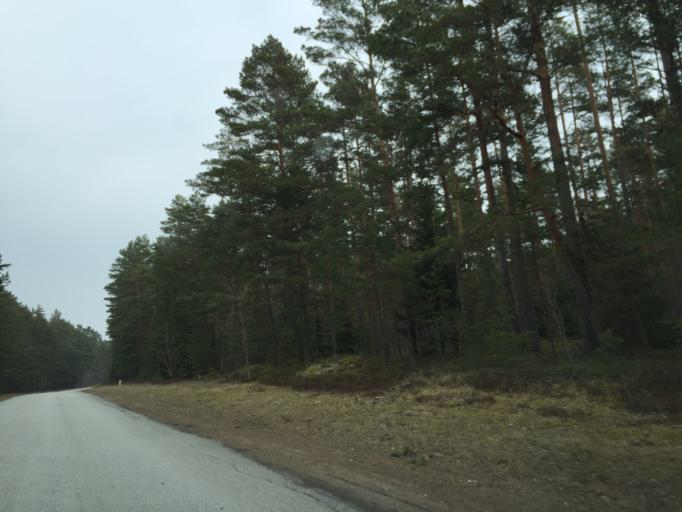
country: LV
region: Salacgrivas
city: Ainazi
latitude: 57.9823
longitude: 24.4171
